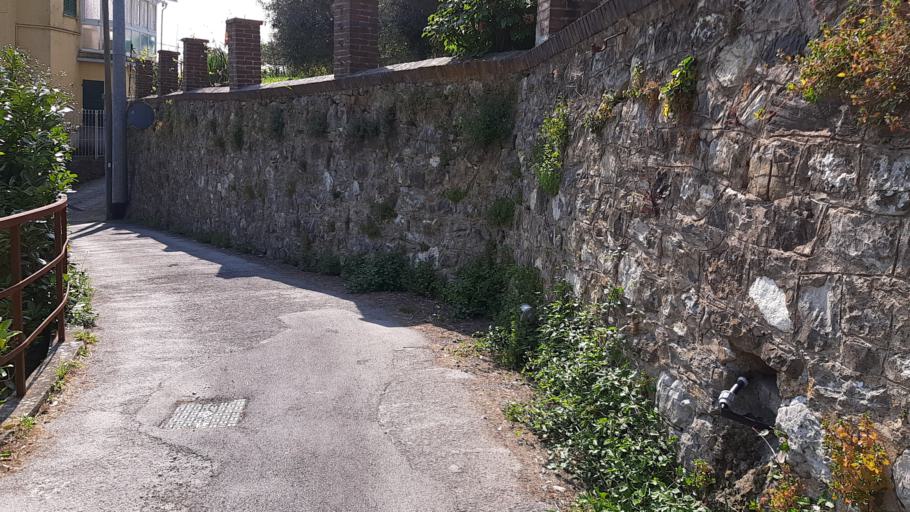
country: IT
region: Liguria
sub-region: Provincia di Genova
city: Bogliasco
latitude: 44.4243
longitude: 9.0147
